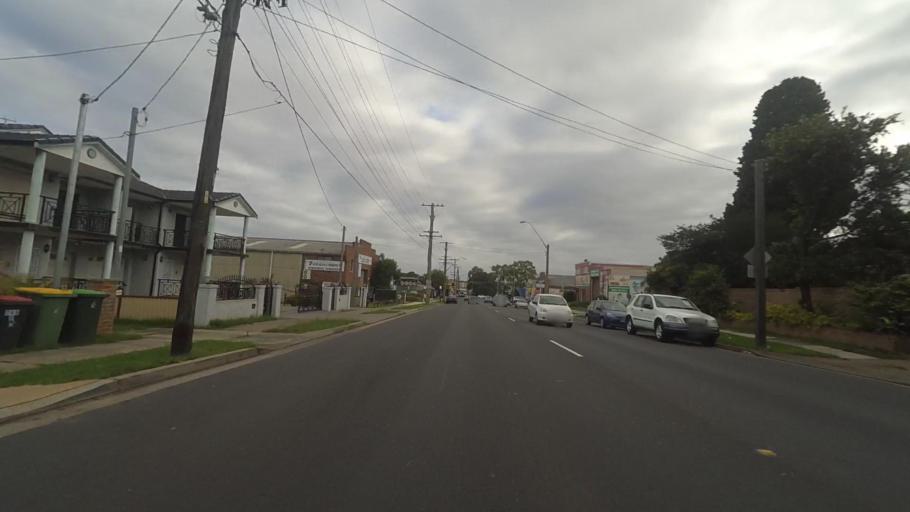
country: AU
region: New South Wales
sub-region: Bankstown
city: Revesby
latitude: -33.9295
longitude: 151.0119
